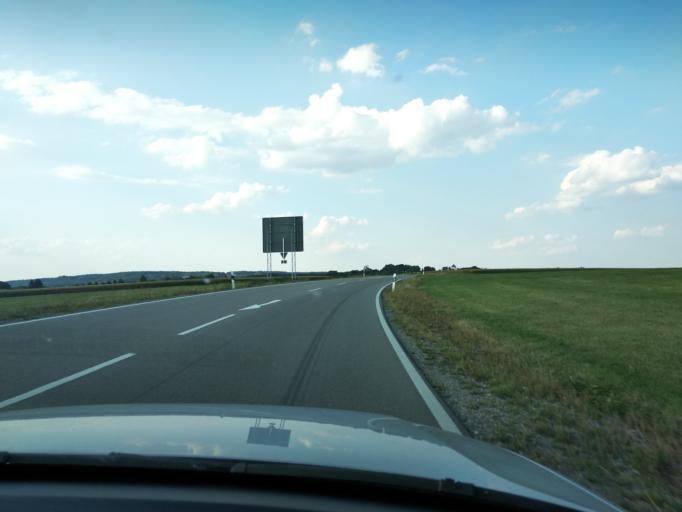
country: DE
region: Bavaria
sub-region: Swabia
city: Trunkelsberg
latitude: 47.9932
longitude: 10.2171
